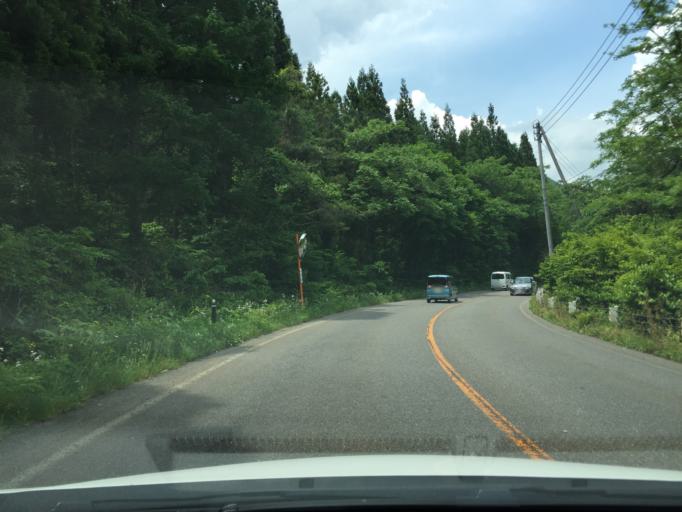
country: JP
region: Fukushima
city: Inawashiro
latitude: 37.6264
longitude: 140.1050
